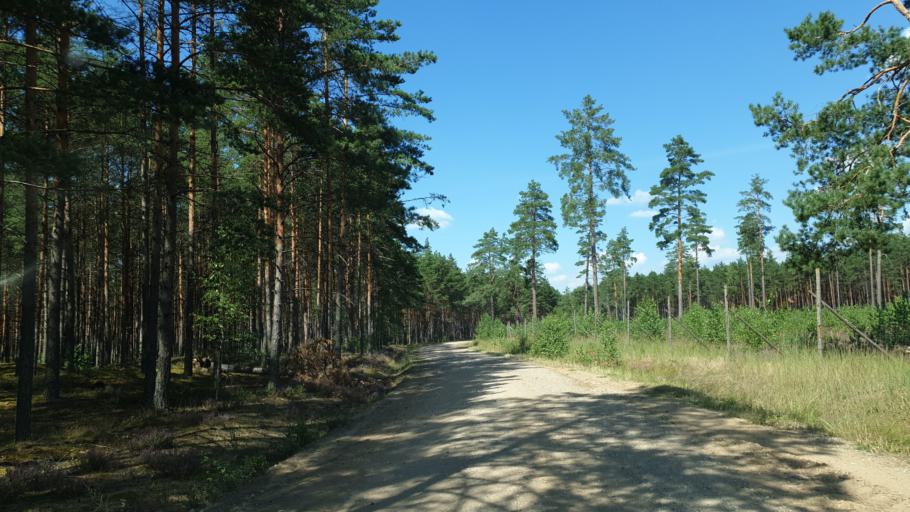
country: LT
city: Sirvintos
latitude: 54.9014
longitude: 24.9572
